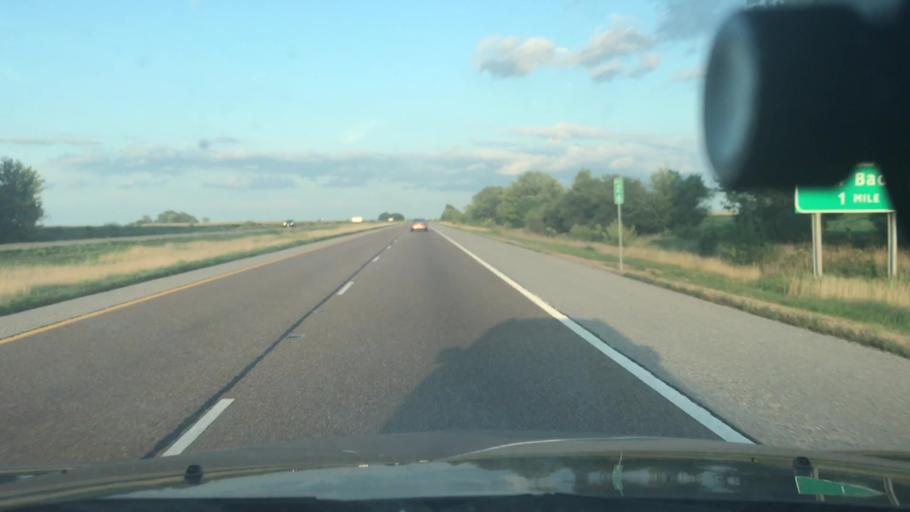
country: US
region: Illinois
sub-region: Clinton County
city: New Baden
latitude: 38.5452
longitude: -89.7488
